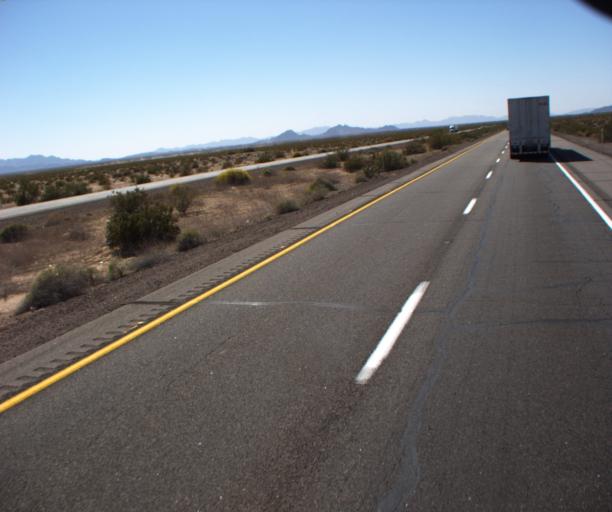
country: US
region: Arizona
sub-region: Yuma County
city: Wellton
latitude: 32.7115
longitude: -113.8361
